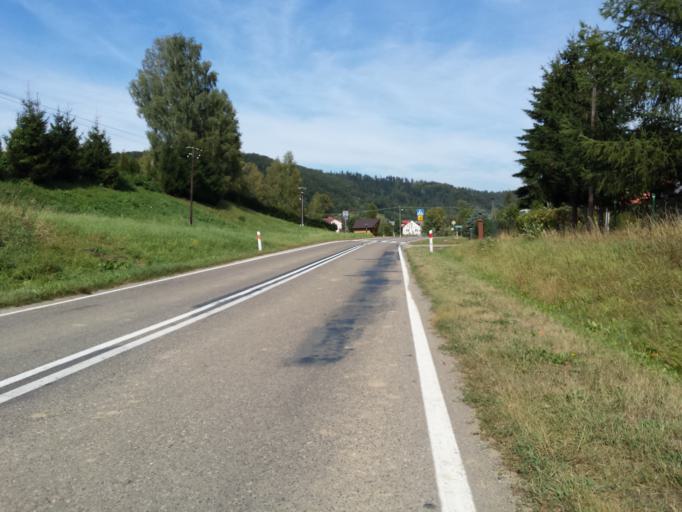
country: PL
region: Subcarpathian Voivodeship
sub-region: Powiat leski
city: Baligrod
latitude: 49.3897
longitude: 22.2859
